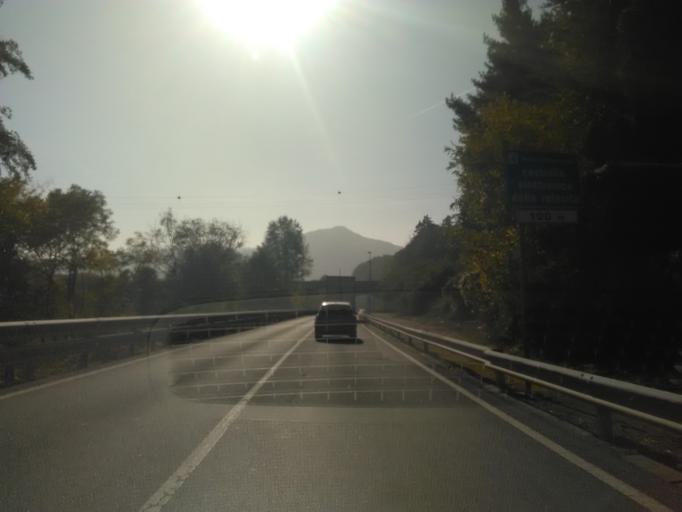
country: IT
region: Piedmont
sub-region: Provincia di Vercelli
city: Borgosesia
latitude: 45.7260
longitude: 8.2619
